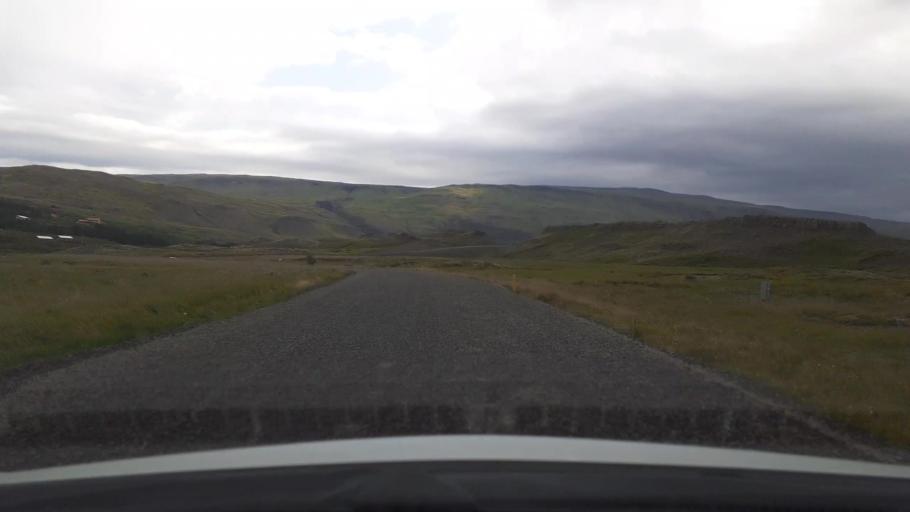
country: IS
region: Capital Region
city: Mosfellsbaer
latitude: 64.2917
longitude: -21.4568
